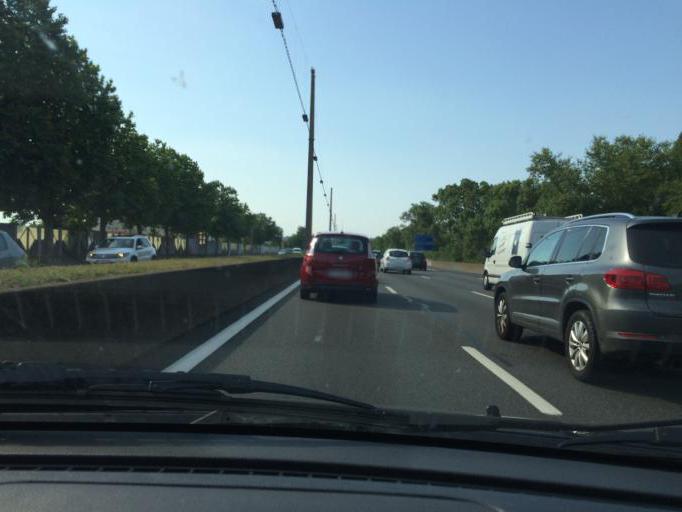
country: FR
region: Rhone-Alpes
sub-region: Departement du Rhone
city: Villeurbanne
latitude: 45.7747
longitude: 4.8989
